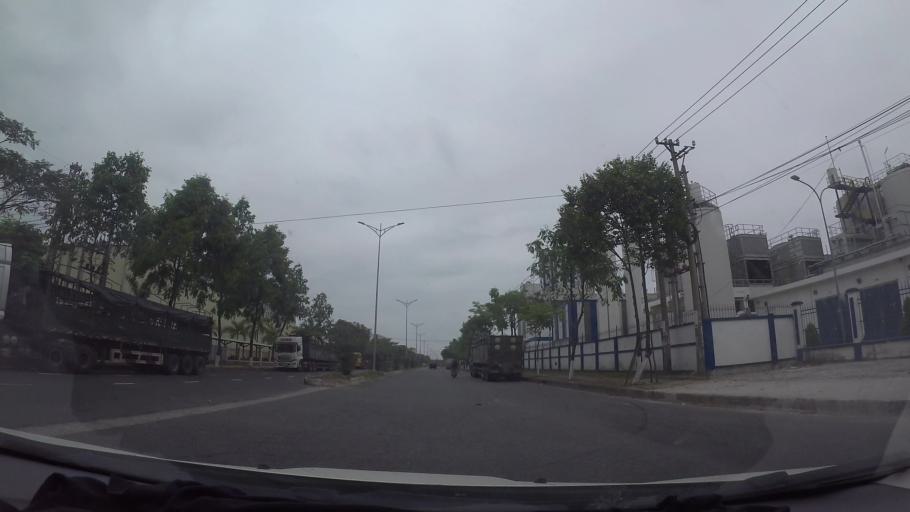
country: VN
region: Da Nang
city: Lien Chieu
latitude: 16.0796
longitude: 108.1419
